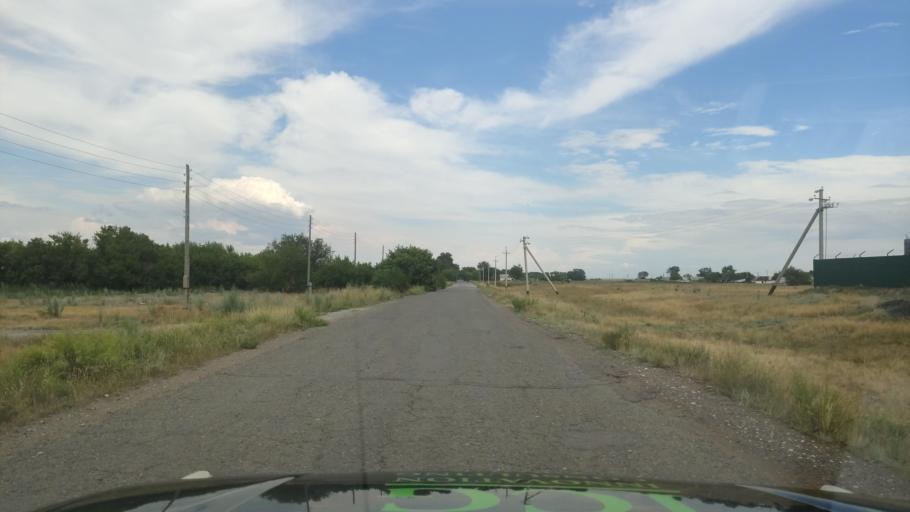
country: KZ
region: Pavlodar
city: Pavlodar
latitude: 52.6610
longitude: 77.4989
